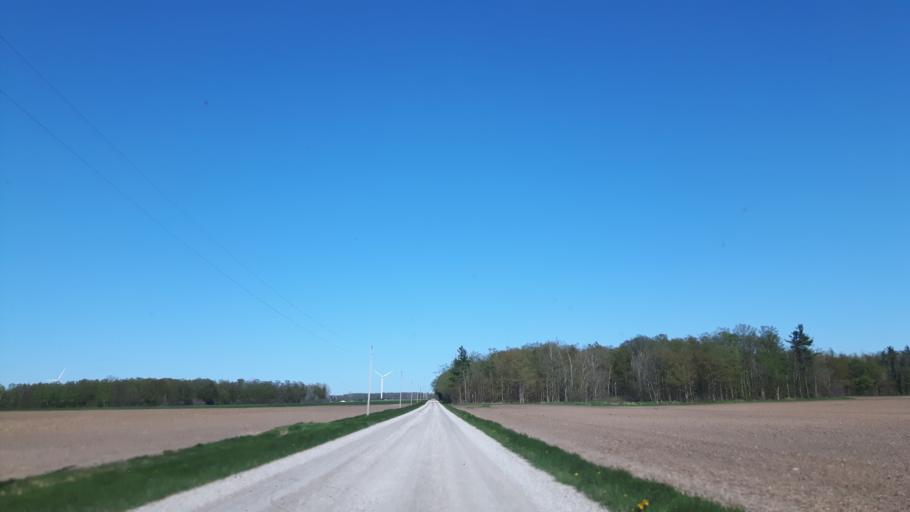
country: CA
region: Ontario
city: Bluewater
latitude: 43.5099
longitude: -81.6922
